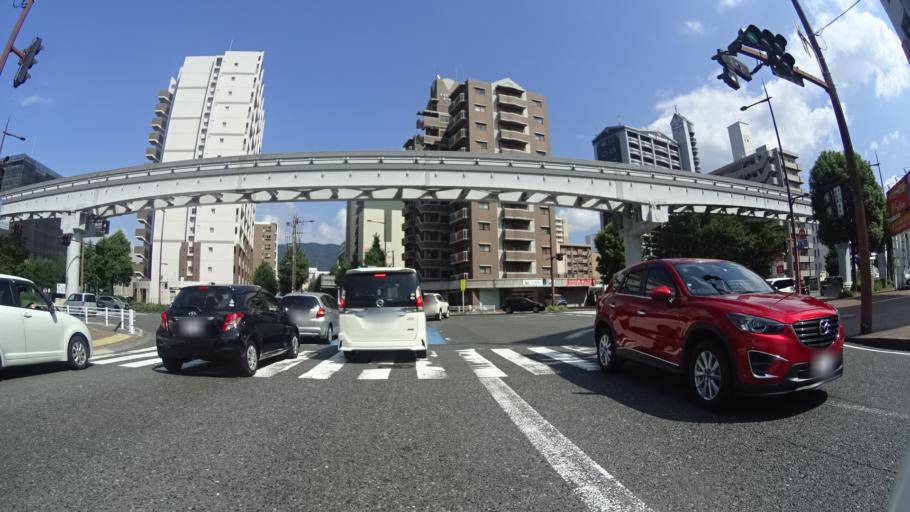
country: JP
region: Fukuoka
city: Kitakyushu
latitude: 33.8646
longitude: 130.8795
